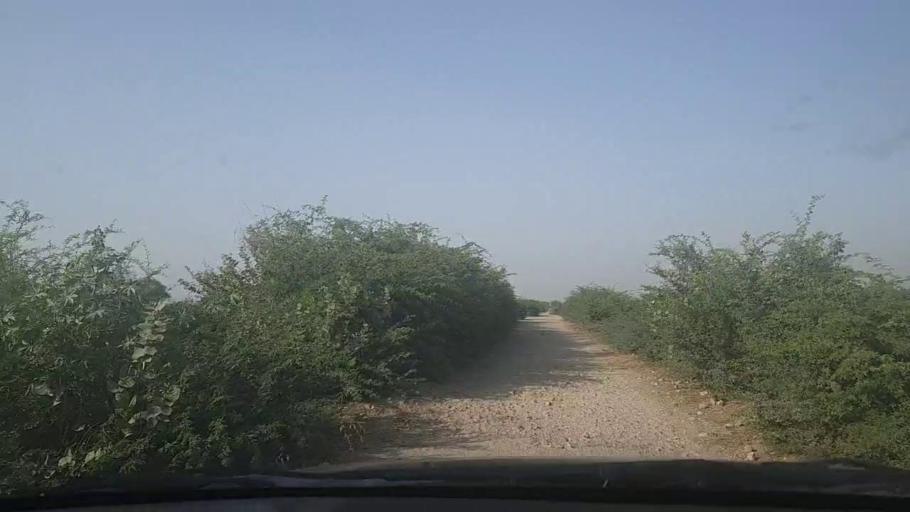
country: PK
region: Sindh
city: Keti Bandar
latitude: 24.2541
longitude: 67.5624
